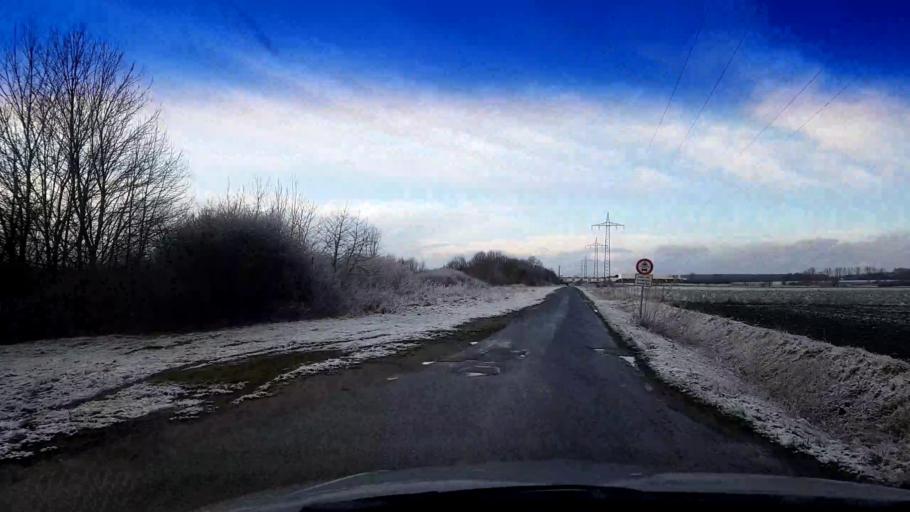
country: DE
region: Bavaria
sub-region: Upper Franconia
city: Altendorf
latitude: 49.8084
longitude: 11.0109
